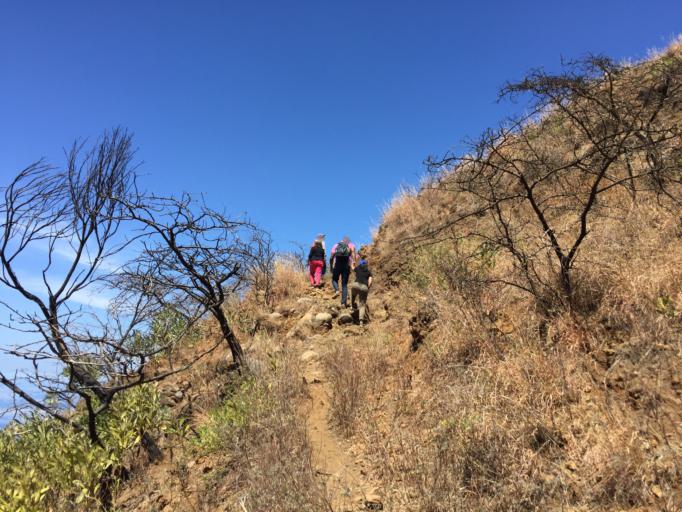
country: CV
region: Mosteiros
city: Porto dos Mosteiros
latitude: 15.0059
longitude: -24.3755
